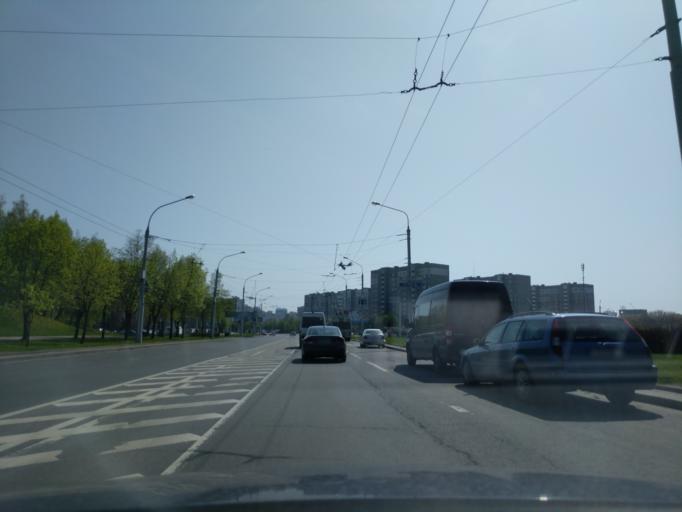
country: BY
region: Minsk
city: Malinovka
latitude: 53.8610
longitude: 27.4612
